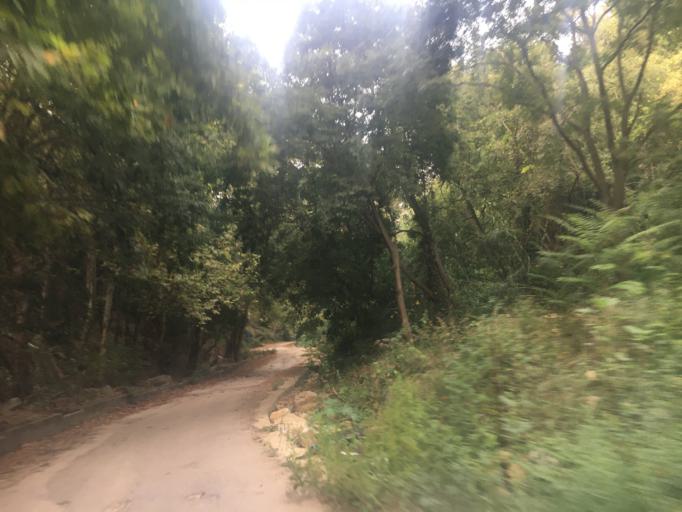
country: LB
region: Mont-Liban
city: Djounie
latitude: 33.9672
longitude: 35.6440
